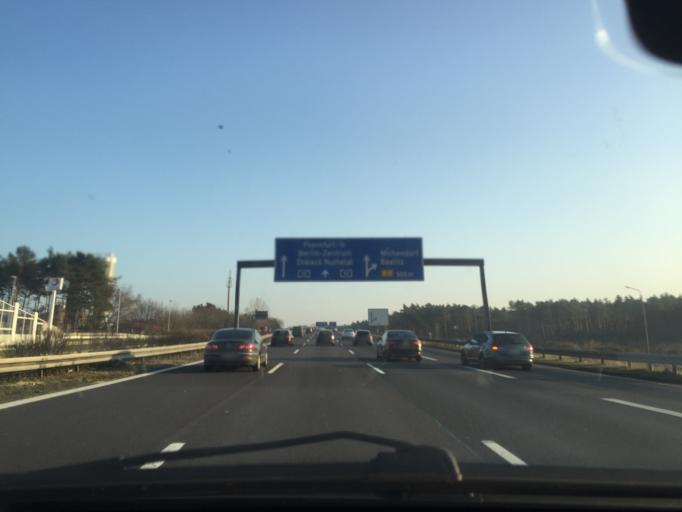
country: DE
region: Brandenburg
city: Michendorf
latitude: 52.3017
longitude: 13.0197
